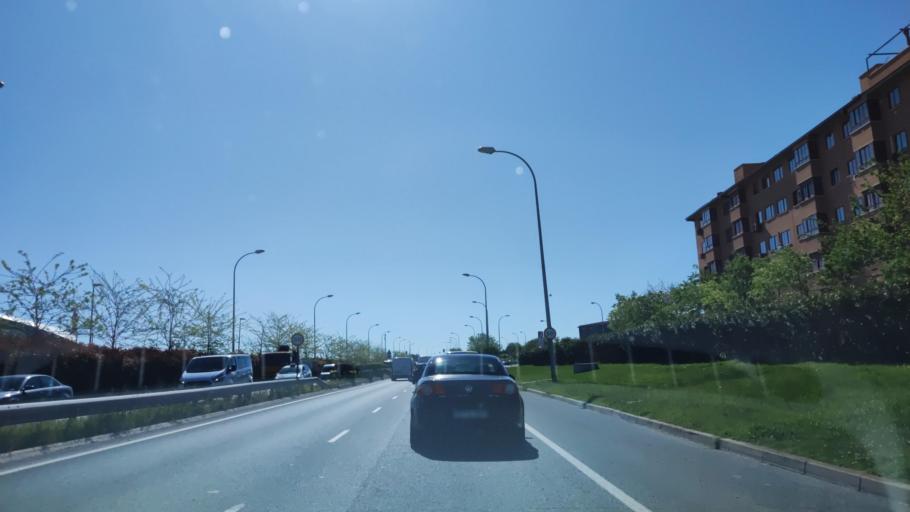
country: ES
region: Madrid
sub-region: Provincia de Madrid
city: San Blas
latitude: 40.4347
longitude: -3.6060
